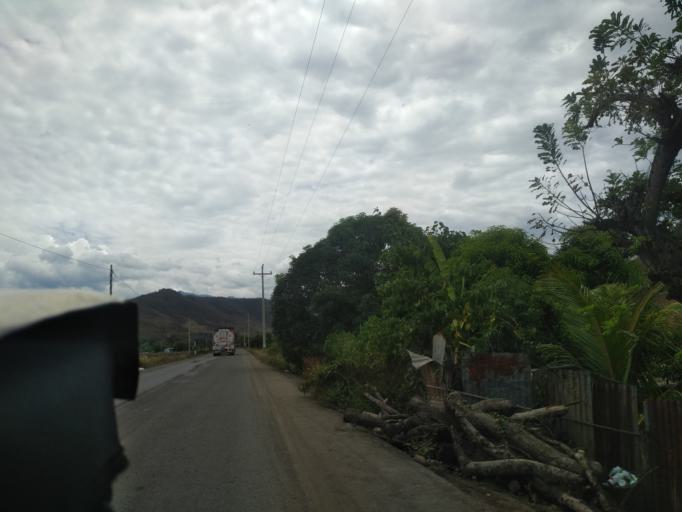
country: PE
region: Cajamarca
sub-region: Provincia de San Ignacio
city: La Coipa
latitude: -5.4233
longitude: -78.7874
